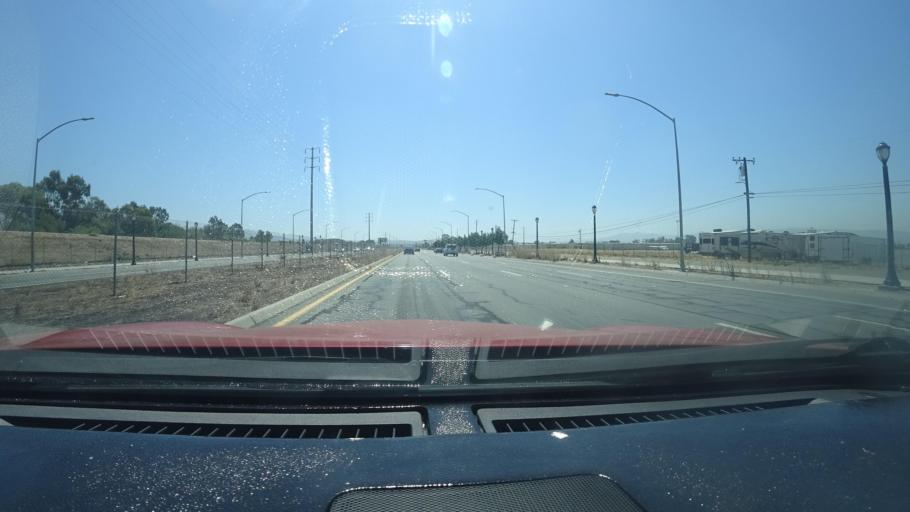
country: US
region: California
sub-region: Santa Clara County
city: Alum Rock
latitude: 37.3357
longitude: -121.8160
